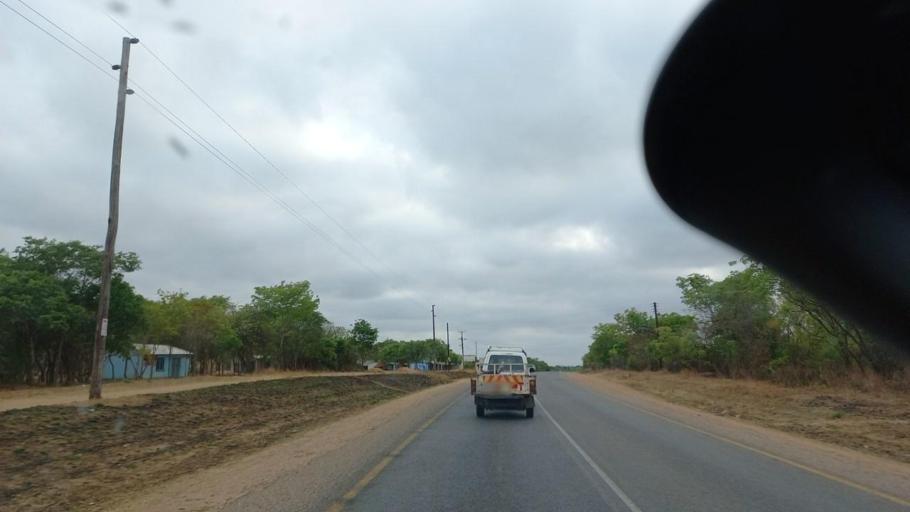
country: ZM
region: Lusaka
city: Chongwe
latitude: -15.2822
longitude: 28.7287
